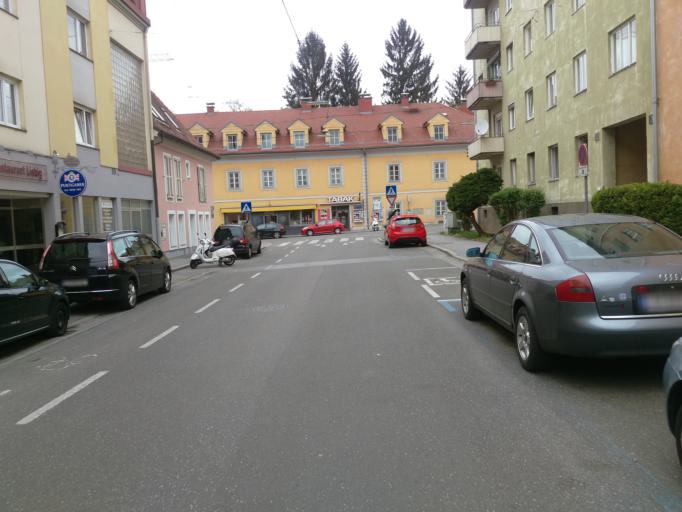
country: AT
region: Styria
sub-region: Graz Stadt
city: Graz
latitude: 47.0801
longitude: 15.4512
